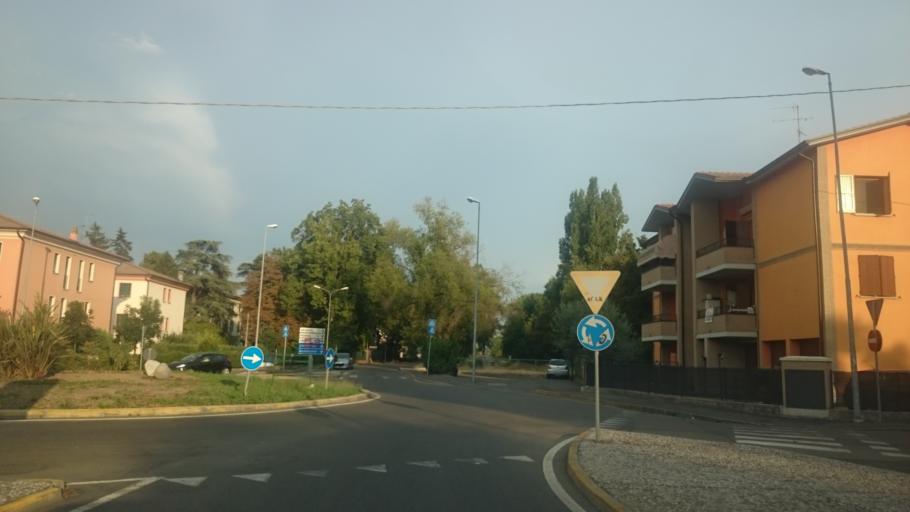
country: IT
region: Emilia-Romagna
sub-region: Provincia di Reggio Emilia
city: Reggio nell'Emilia
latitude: 44.7098
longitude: 10.6456
